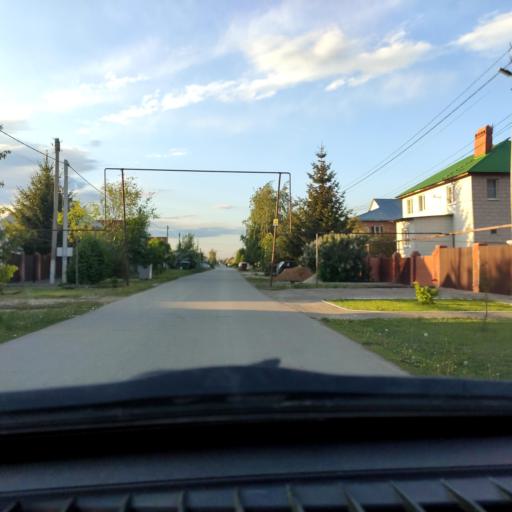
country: RU
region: Samara
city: Tol'yatti
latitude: 53.5612
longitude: 49.4025
